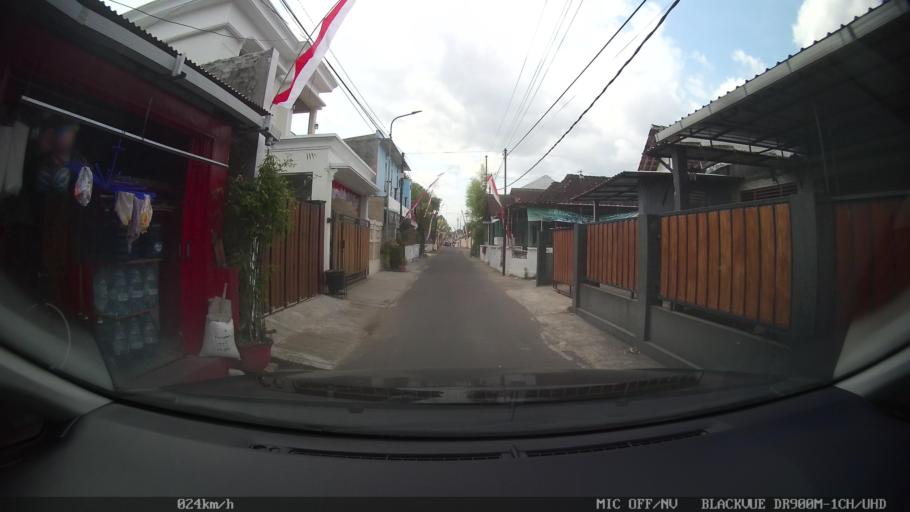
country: ID
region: Daerah Istimewa Yogyakarta
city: Gamping Lor
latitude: -7.8026
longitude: 110.3383
